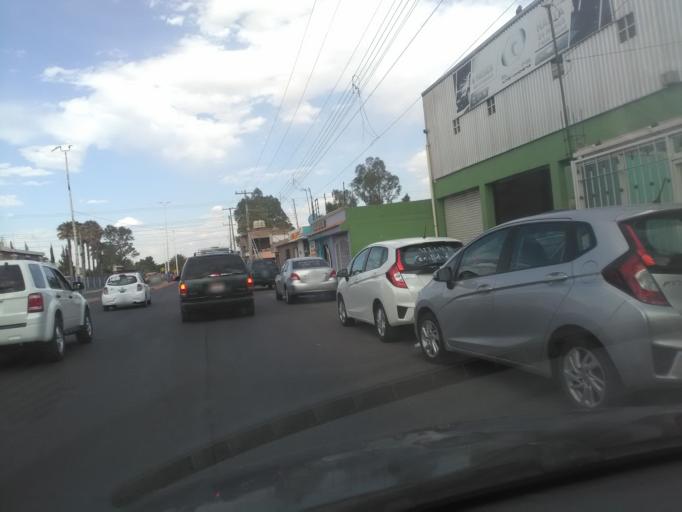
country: MX
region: Durango
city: Victoria de Durango
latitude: 24.0198
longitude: -104.6413
